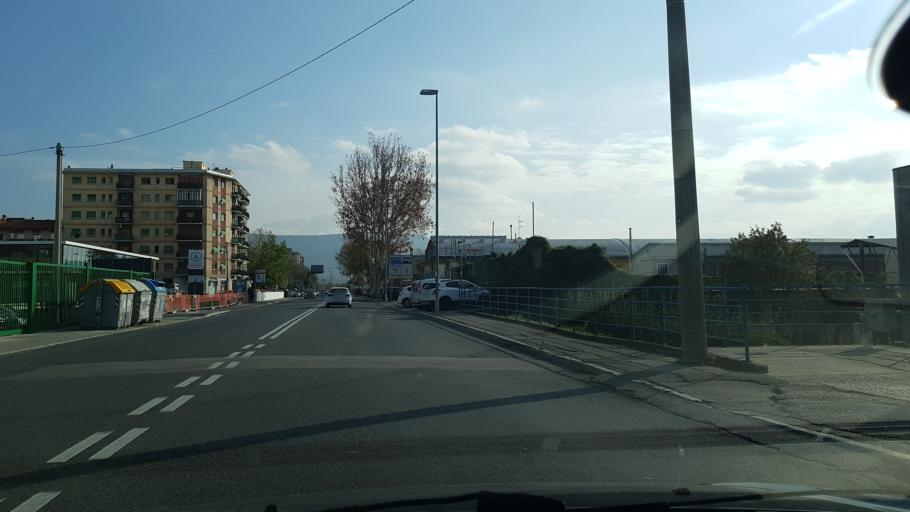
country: IT
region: Friuli Venezia Giulia
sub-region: Provincia di Trieste
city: Domio
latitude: 45.6210
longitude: 13.8084
